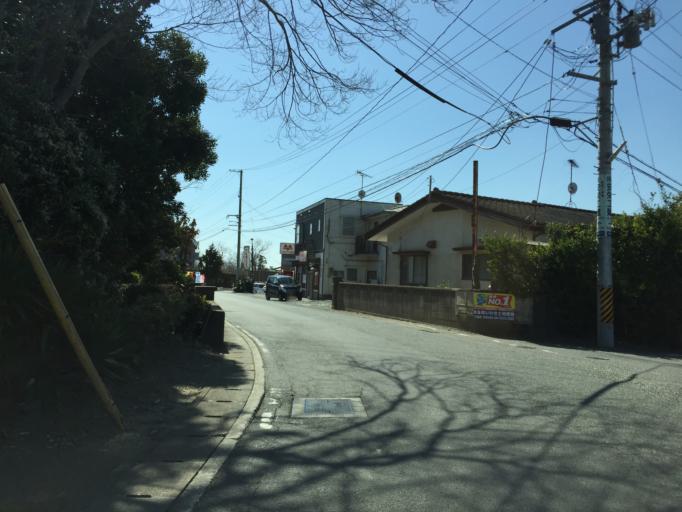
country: JP
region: Fukushima
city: Iwaki
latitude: 37.0537
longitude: 140.8409
